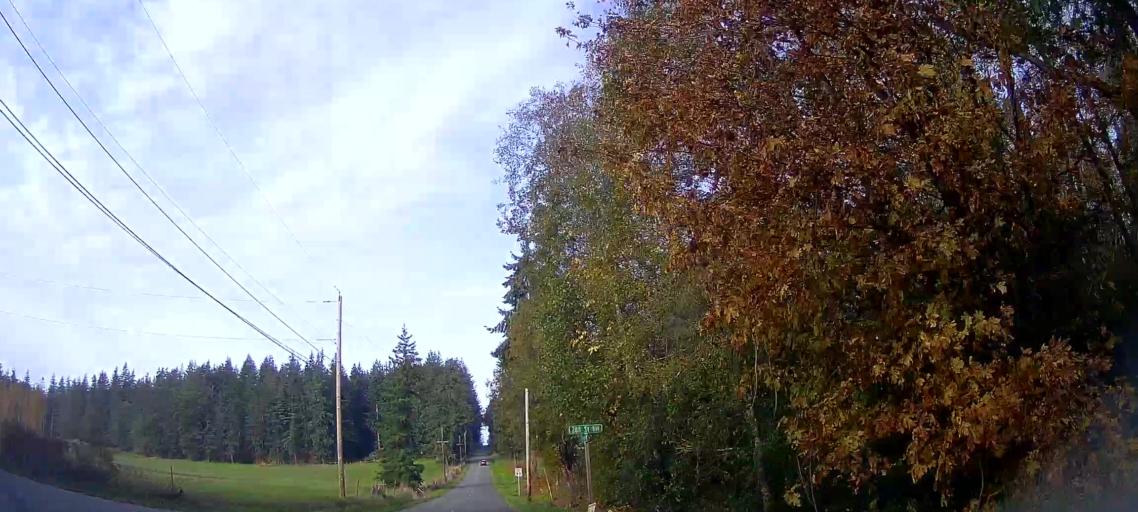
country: US
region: Washington
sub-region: Snohomish County
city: Stanwood
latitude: 48.2589
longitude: -122.3414
